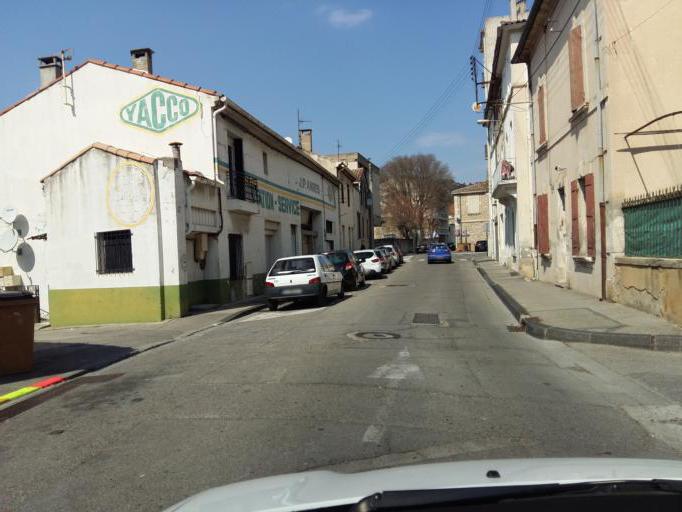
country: FR
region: Provence-Alpes-Cote d'Azur
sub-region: Departement du Vaucluse
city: Cavaillon
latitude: 43.8330
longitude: 5.0370
